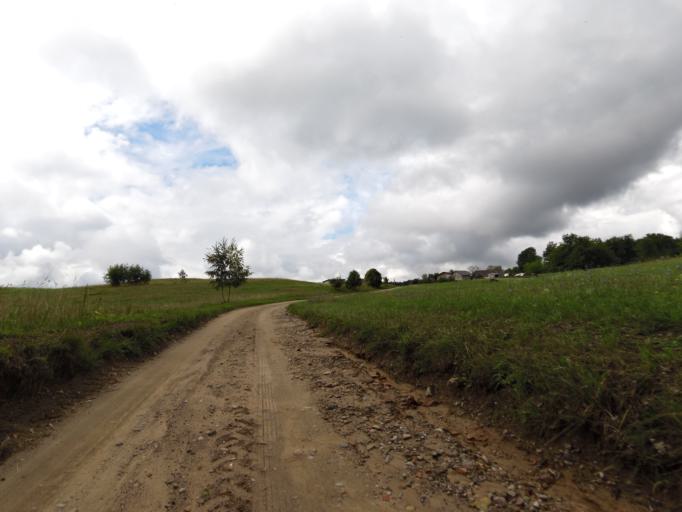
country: LT
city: Grigiskes
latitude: 54.7035
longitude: 25.1148
